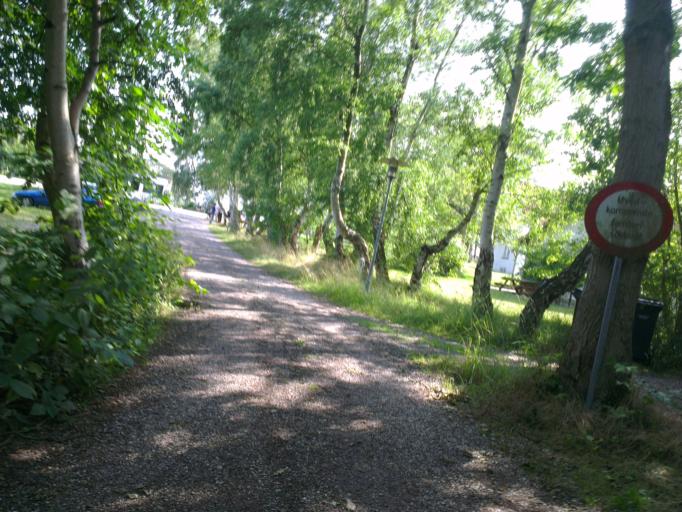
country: DK
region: Capital Region
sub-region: Frederikssund Kommune
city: Jaegerspris
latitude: 55.9080
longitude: 11.9170
